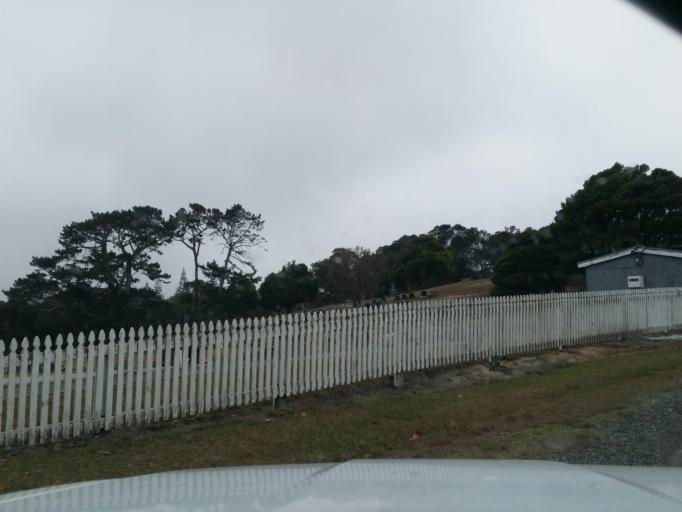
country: NZ
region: Northland
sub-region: Kaipara District
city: Dargaville
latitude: -35.9649
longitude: 173.8607
